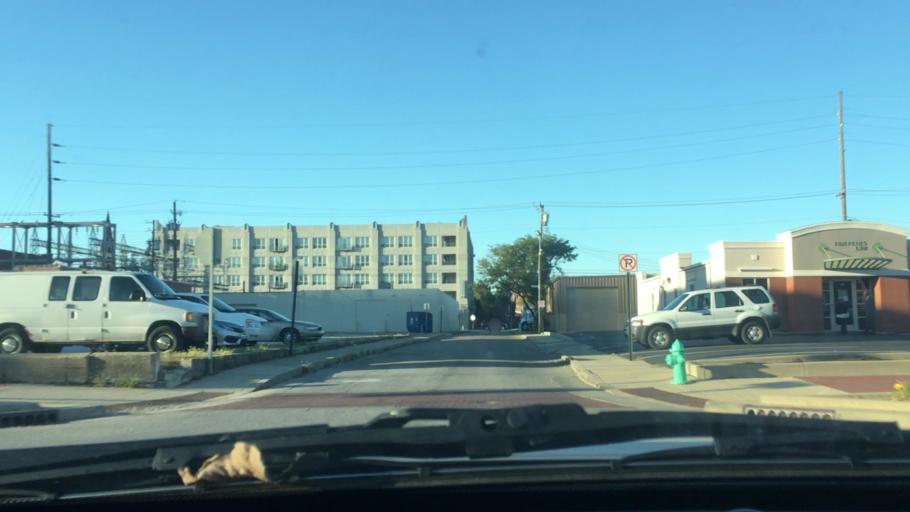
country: US
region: Indiana
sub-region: Marion County
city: Indianapolis
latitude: 39.7682
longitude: -86.1472
